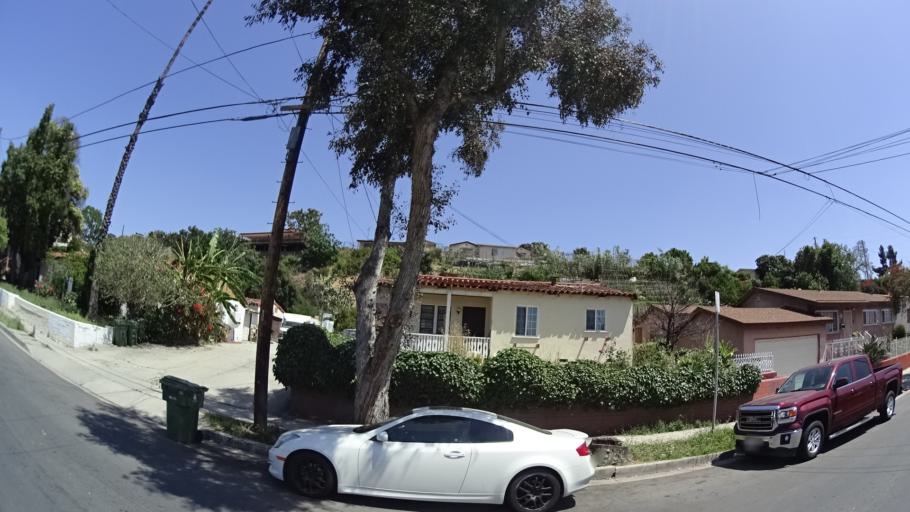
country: US
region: California
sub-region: Los Angeles County
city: Boyle Heights
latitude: 34.0689
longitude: -118.2052
